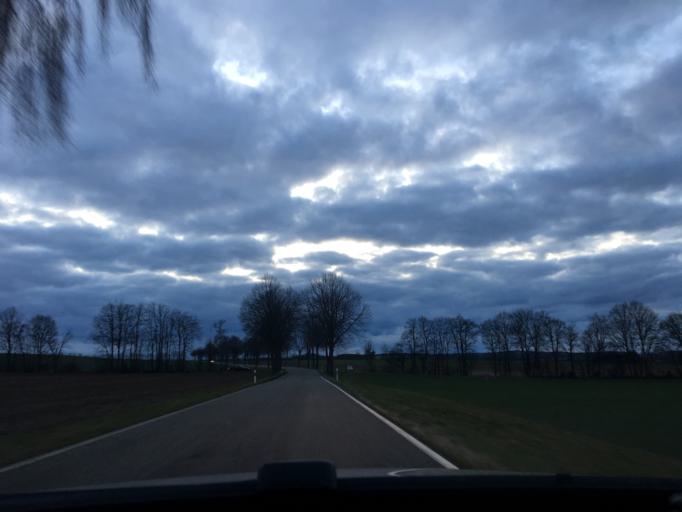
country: DE
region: Rheinland-Pfalz
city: Erbes-Budesheim
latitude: 49.7548
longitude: 8.0242
